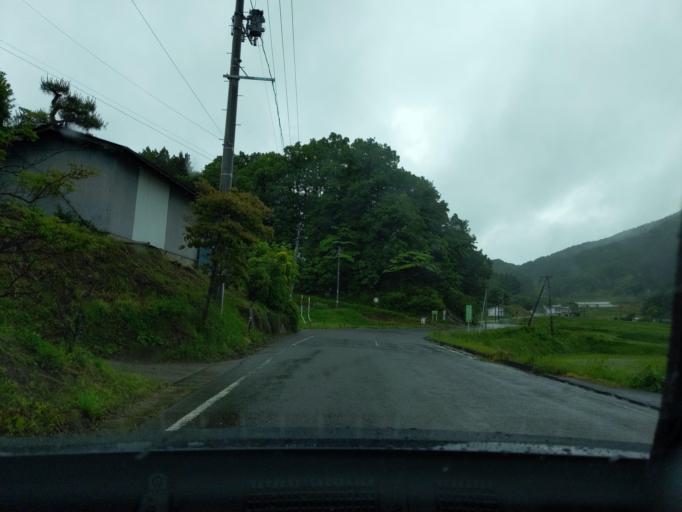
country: JP
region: Fukushima
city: Funehikimachi-funehiki
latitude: 37.5966
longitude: 140.5826
